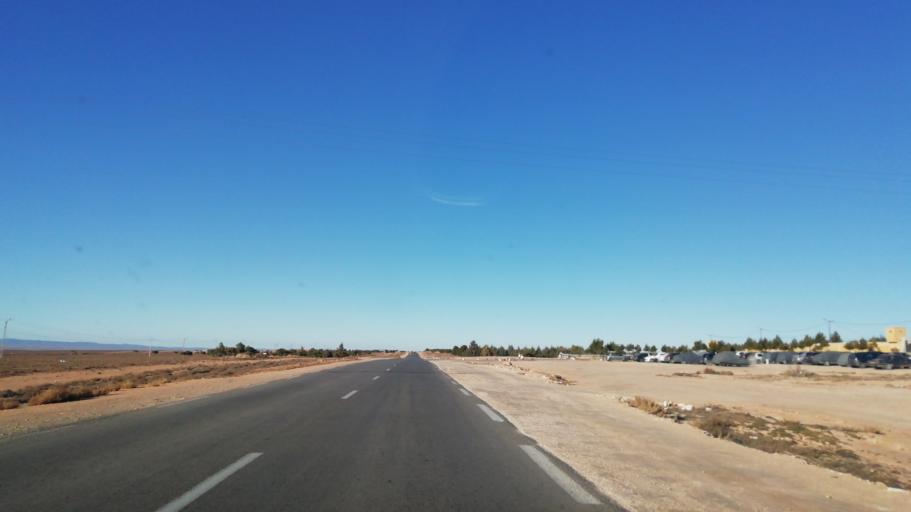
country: DZ
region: Tlemcen
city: Sebdou
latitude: 34.2670
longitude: -1.2582
